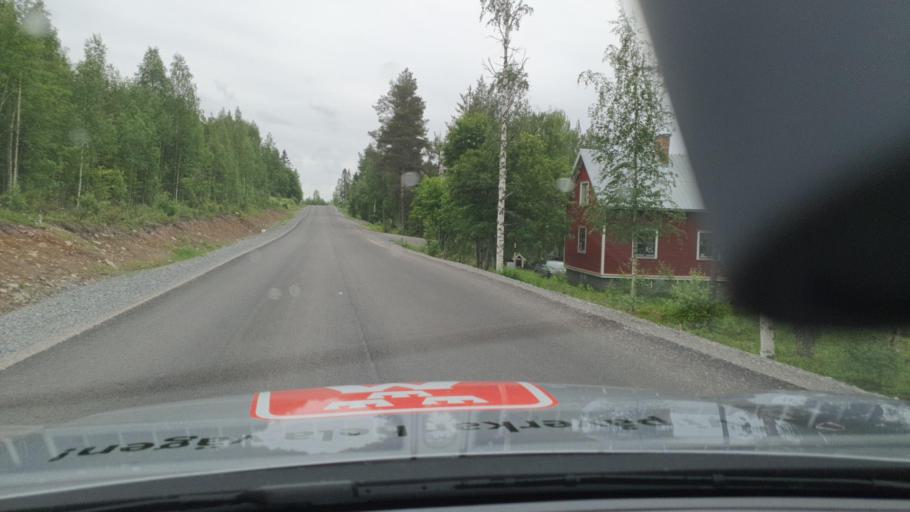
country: SE
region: Norrbotten
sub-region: Overtornea Kommun
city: OEvertornea
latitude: 66.5964
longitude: 23.3081
